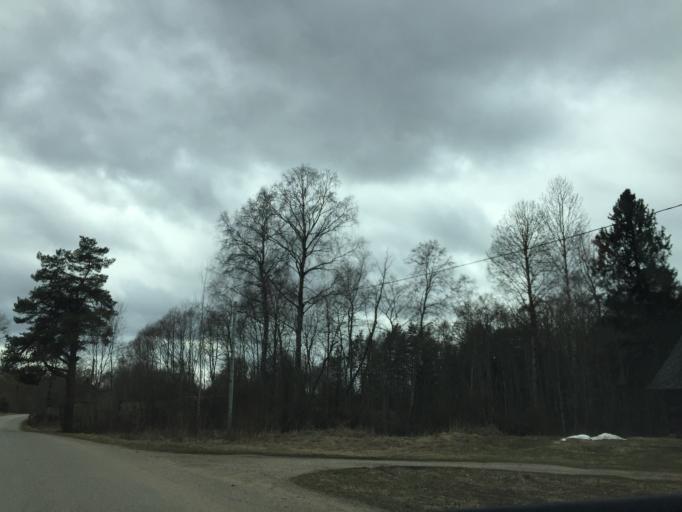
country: LV
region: Kraslavas Rajons
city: Kraslava
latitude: 55.9547
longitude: 27.0151
